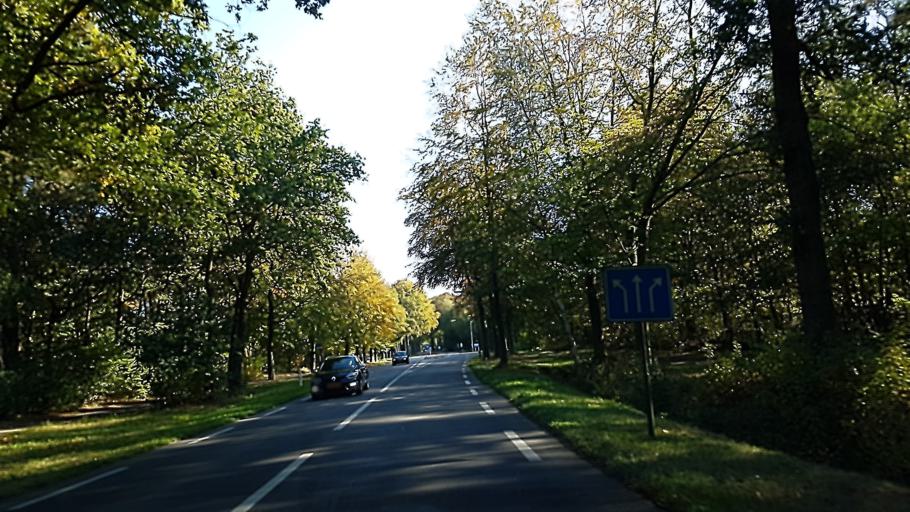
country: BE
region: Flanders
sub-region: Provincie Antwerpen
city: Stabroek
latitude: 51.3843
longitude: 4.3708
